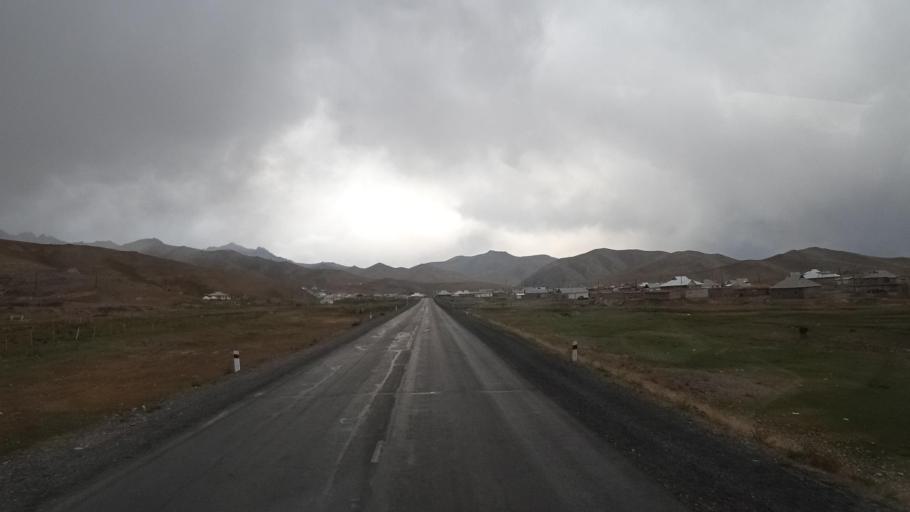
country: KG
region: Osh
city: Gul'cha
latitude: 39.7201
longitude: 73.2451
